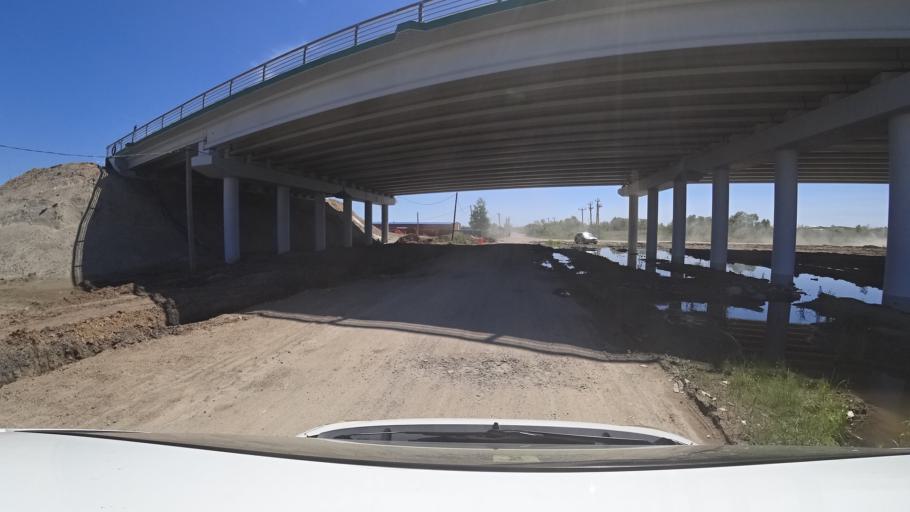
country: RU
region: Khabarovsk Krai
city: Topolevo
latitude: 48.4821
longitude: 135.1746
